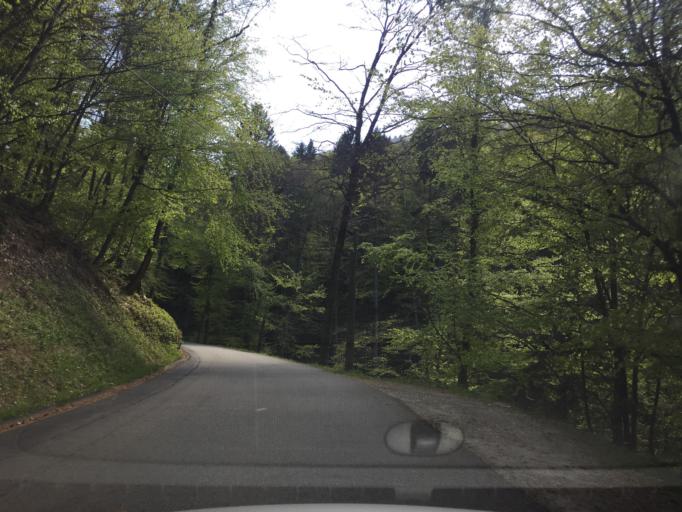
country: FR
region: Rhone-Alpes
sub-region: Departement de la Savoie
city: Vimines
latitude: 45.5708
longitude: 5.8369
